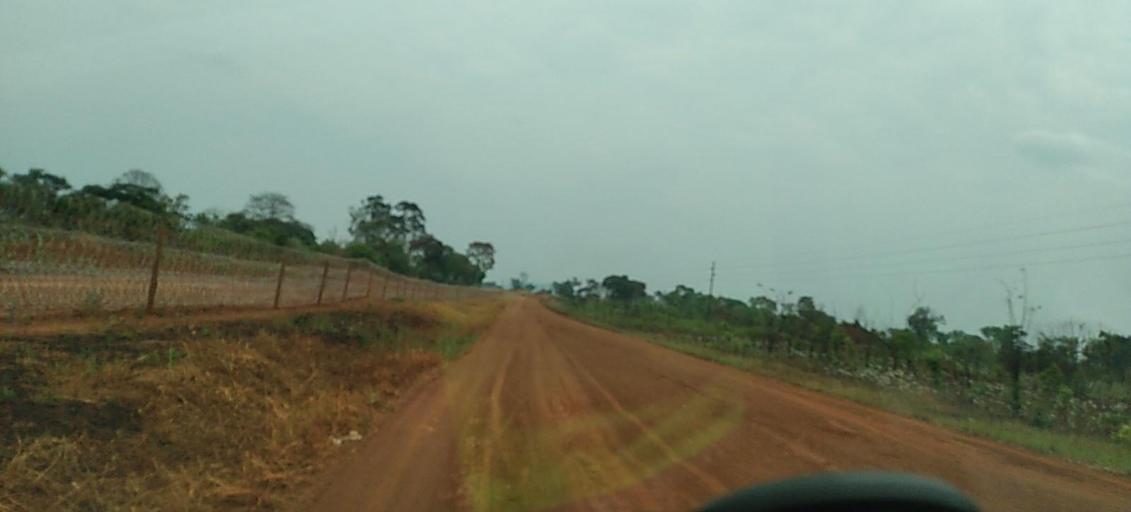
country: ZM
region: North-Western
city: Kansanshi
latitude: -12.0841
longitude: 26.4819
